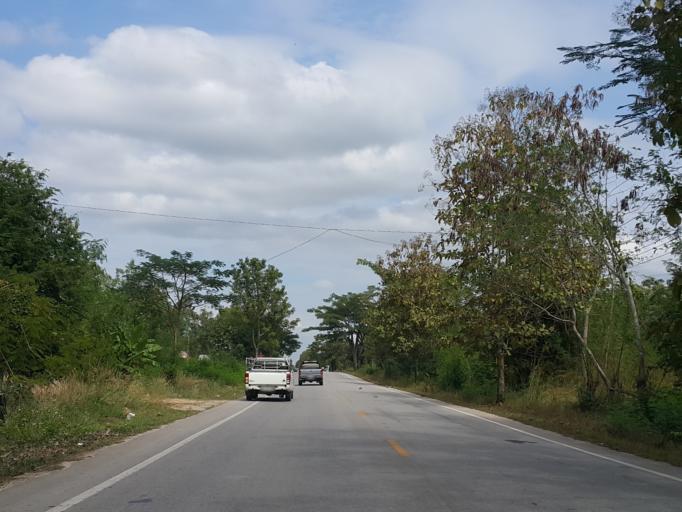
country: TH
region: Lampang
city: Lampang
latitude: 18.3761
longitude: 99.4584
